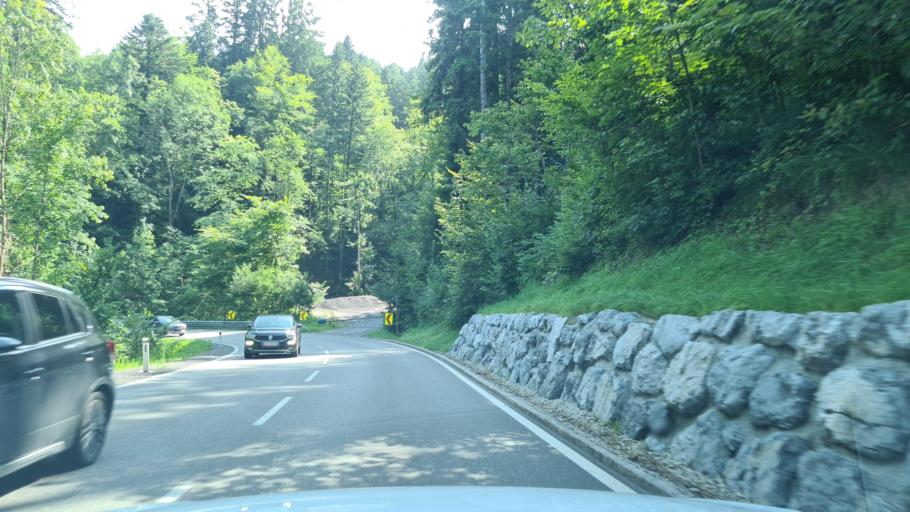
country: AT
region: Vorarlberg
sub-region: Politischer Bezirk Bregenz
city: Egg
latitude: 47.4541
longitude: 9.8704
